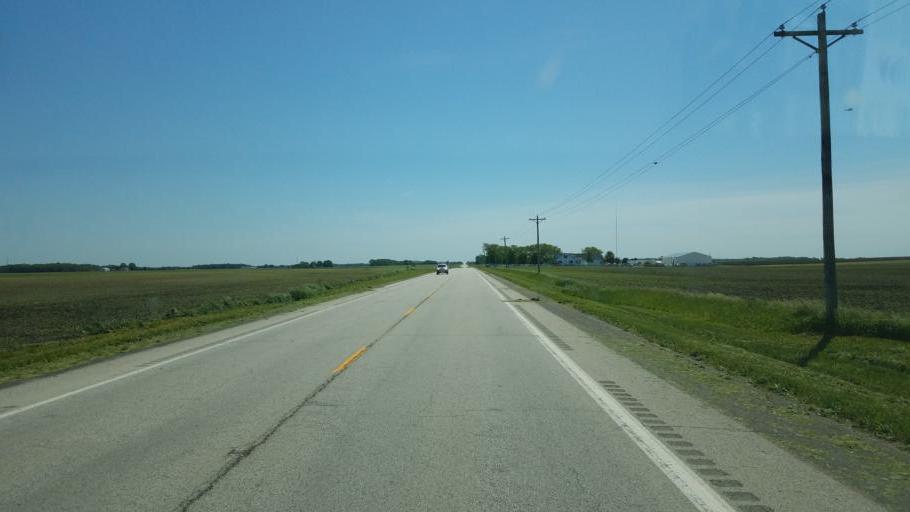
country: US
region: Illinois
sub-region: McLean County
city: Le Roy
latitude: 40.3118
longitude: -88.8137
